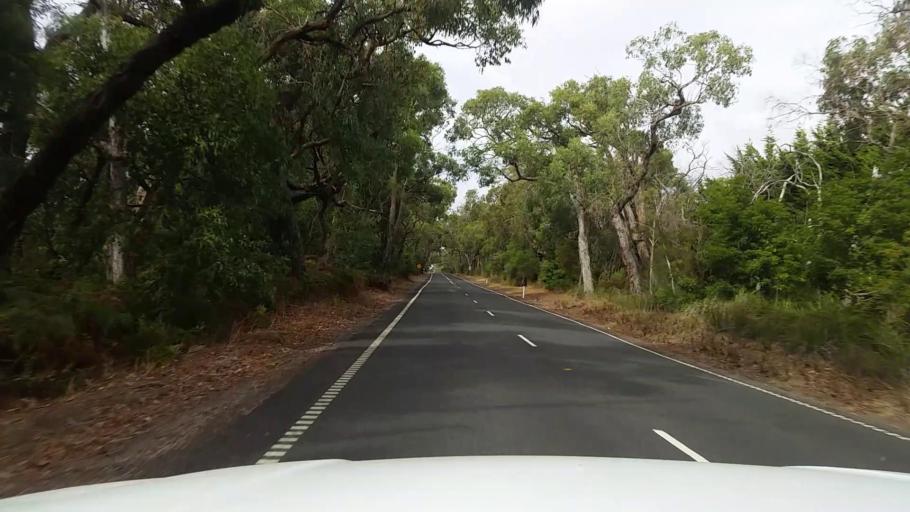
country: AU
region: Victoria
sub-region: Mornington Peninsula
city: Balnarring
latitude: -38.3292
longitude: 145.0938
